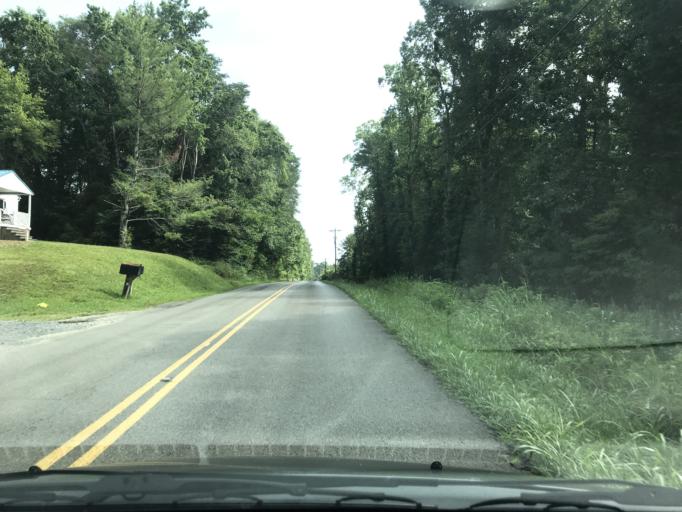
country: US
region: Tennessee
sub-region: Hamilton County
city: Apison
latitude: 35.0746
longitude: -84.9763
